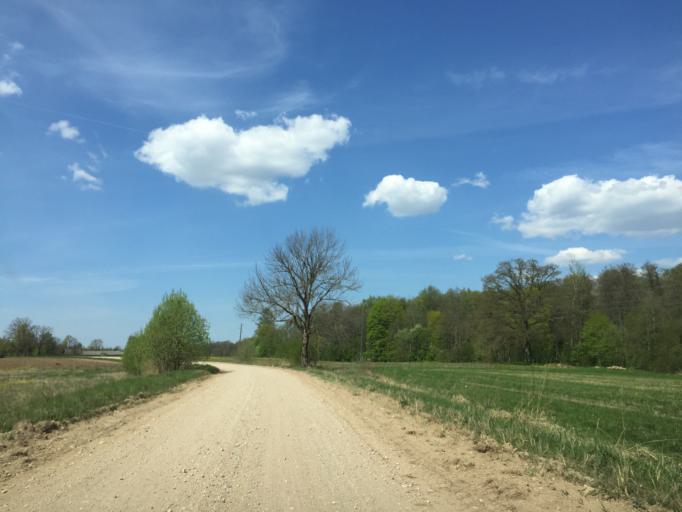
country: LV
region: Limbazu Rajons
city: Limbazi
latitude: 57.3794
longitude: 24.6252
